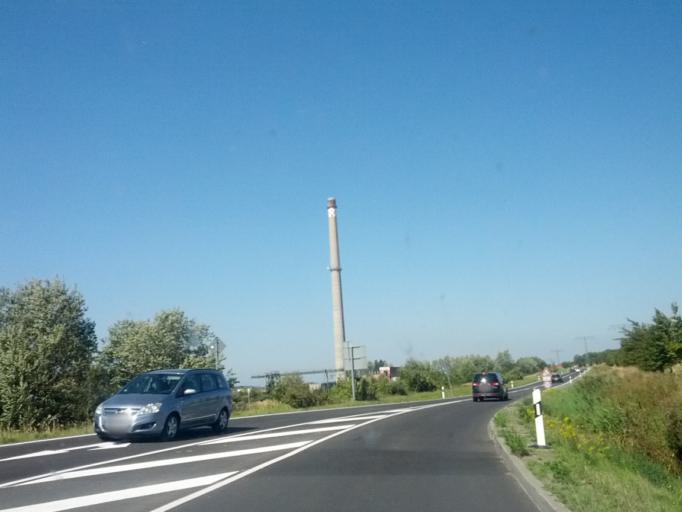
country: DE
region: Mecklenburg-Vorpommern
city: Sagard
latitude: 54.4928
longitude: 13.5777
